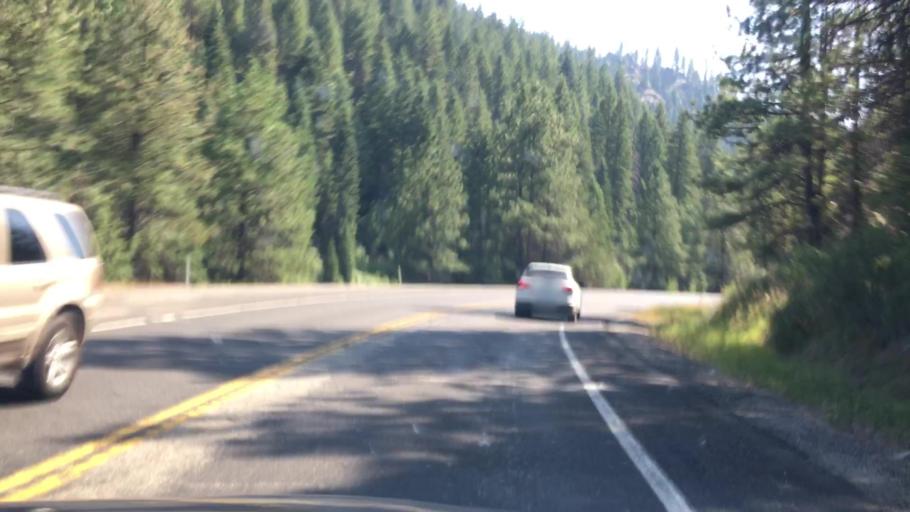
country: US
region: Idaho
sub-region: Valley County
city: Cascade
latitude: 44.2488
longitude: -116.0937
